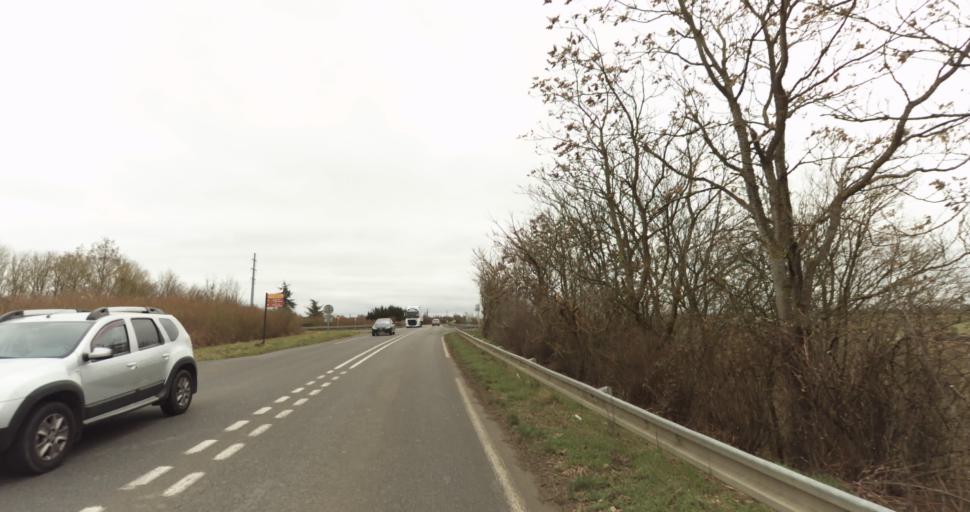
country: FR
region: Pays de la Loire
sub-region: Departement de Maine-et-Loire
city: Doue-la-Fontaine
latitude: 47.1816
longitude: -0.2637
